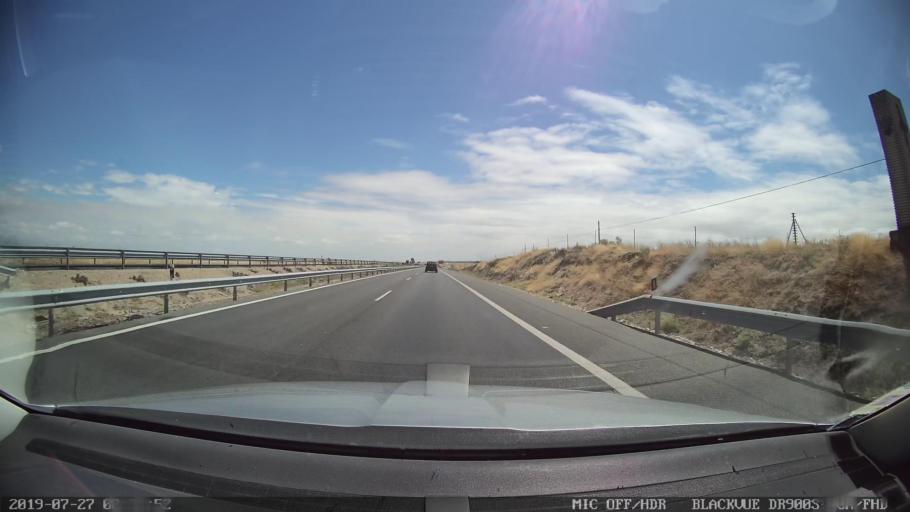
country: ES
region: Extremadura
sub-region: Provincia de Caceres
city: Peraleda de la Mata
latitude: 39.8916
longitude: -5.4002
